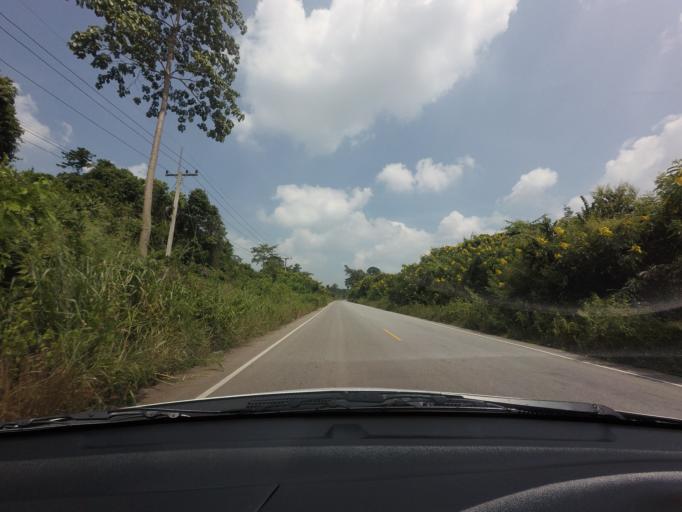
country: TH
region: Nakhon Ratchasima
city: Pak Chong
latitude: 14.5927
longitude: 101.5718
